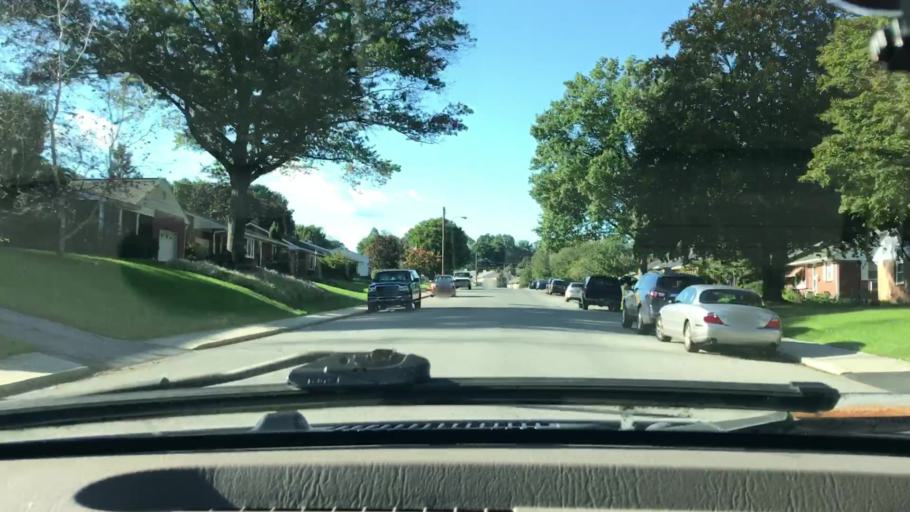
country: US
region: Pennsylvania
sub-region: Lancaster County
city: Elizabethtown
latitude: 40.1593
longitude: -76.6046
